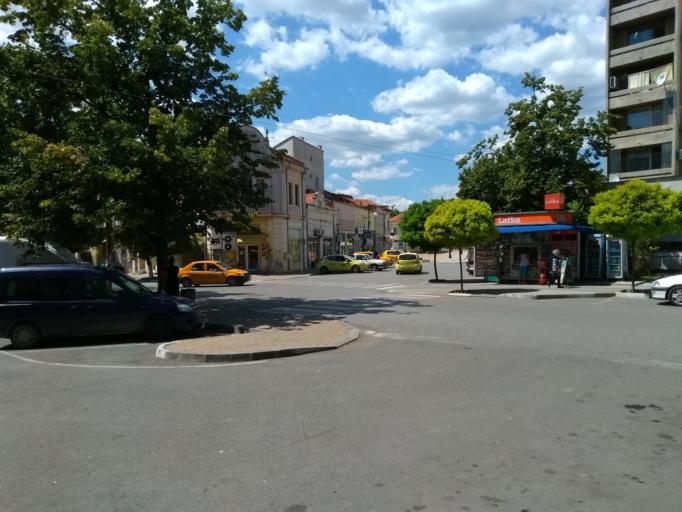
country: BG
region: Sliven
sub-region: Obshtina Nova Zagora
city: Nova Zagora
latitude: 42.4924
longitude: 26.0094
